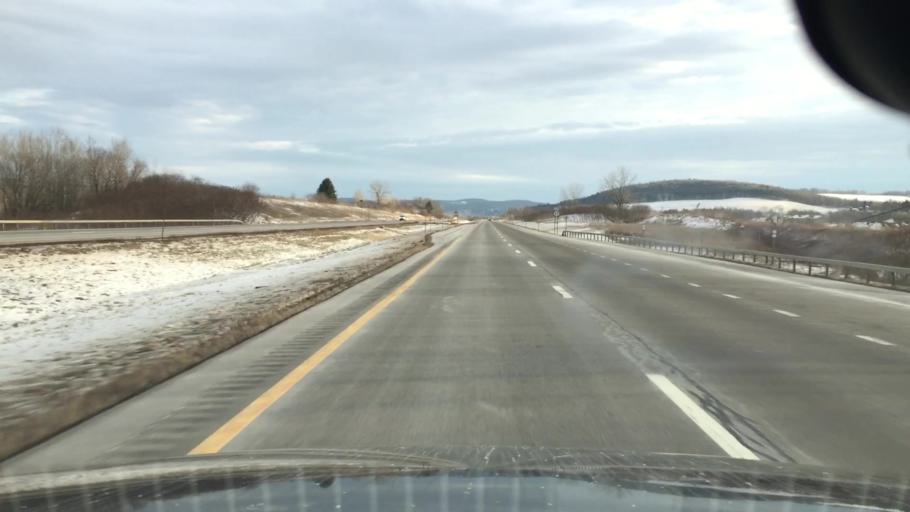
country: US
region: New York
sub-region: Tioga County
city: Owego
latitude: 42.0667
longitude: -76.3232
